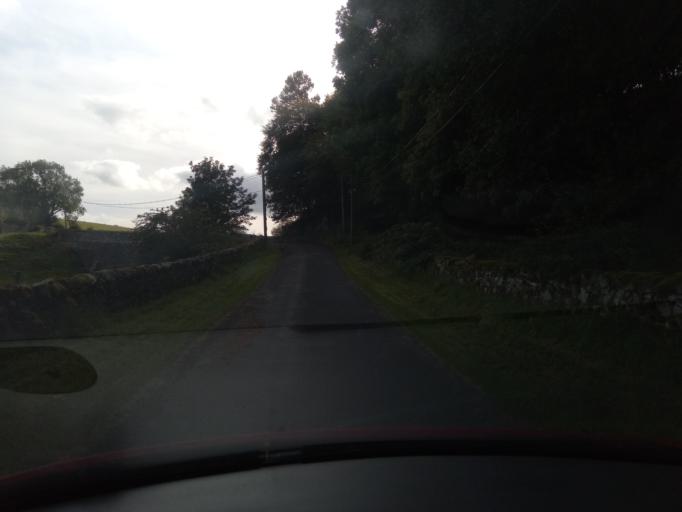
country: GB
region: Scotland
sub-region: The Scottish Borders
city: Kelso
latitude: 55.4791
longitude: -2.3539
